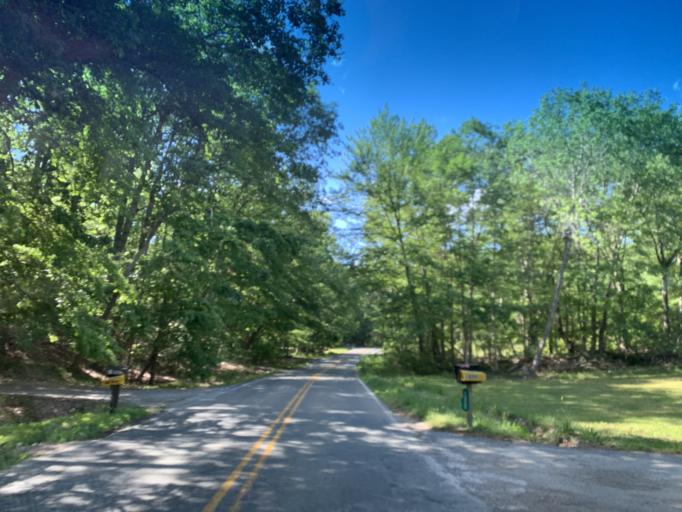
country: US
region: Maryland
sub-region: Cecil County
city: North East
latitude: 39.5522
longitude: -75.9230
